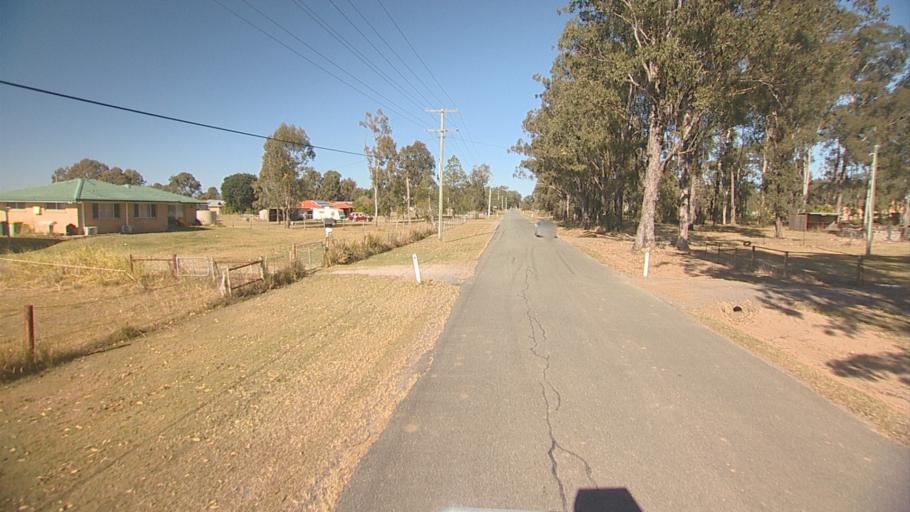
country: AU
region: Queensland
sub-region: Logan
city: Chambers Flat
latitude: -27.7536
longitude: 153.0762
